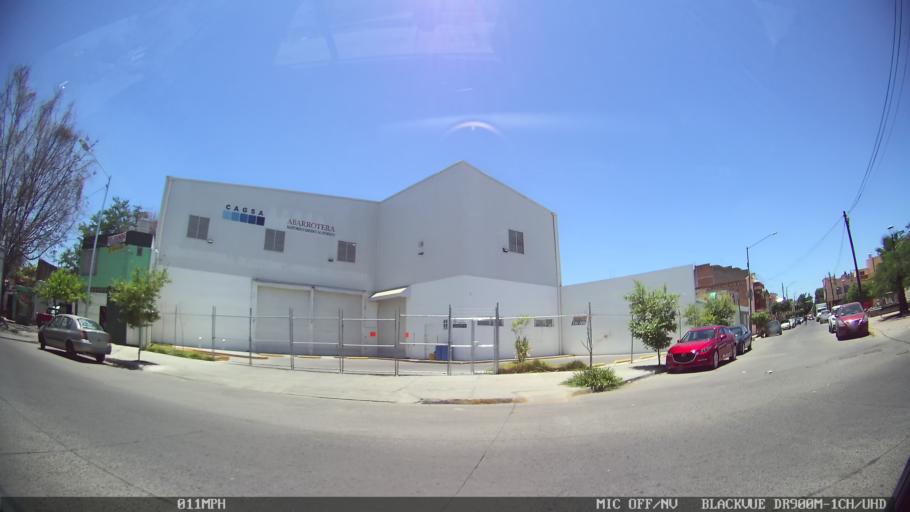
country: MX
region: Jalisco
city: Tlaquepaque
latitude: 20.6632
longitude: -103.2912
